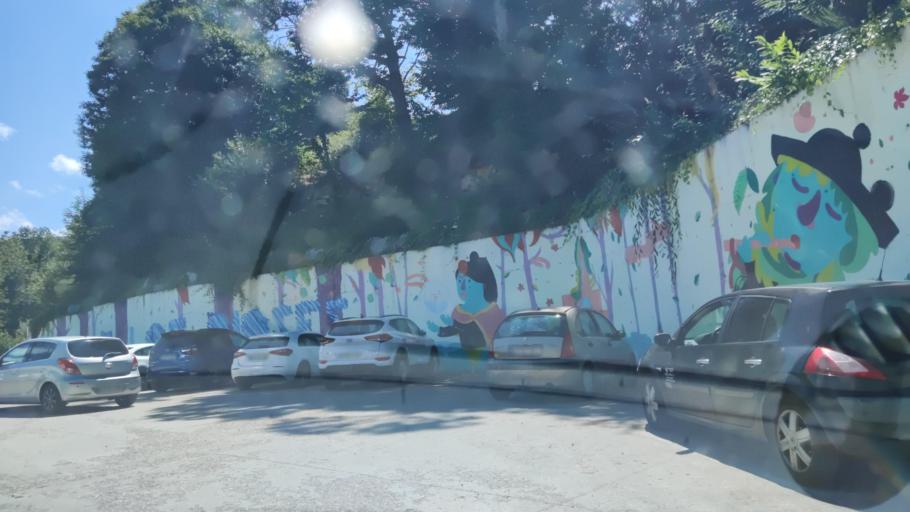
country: ES
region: Castille and Leon
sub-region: Provincia de Salamanca
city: Candelario
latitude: 40.3660
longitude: -5.7473
